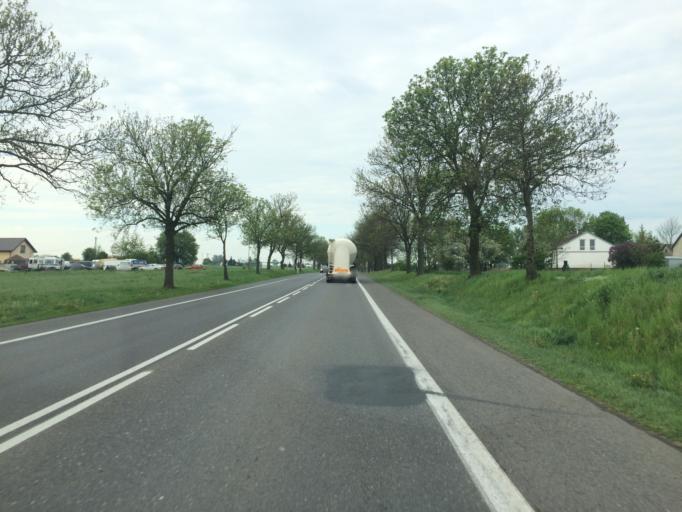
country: PL
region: Masovian Voivodeship
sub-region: Powiat mlawski
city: Wisniewo
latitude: 53.0789
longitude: 20.3543
